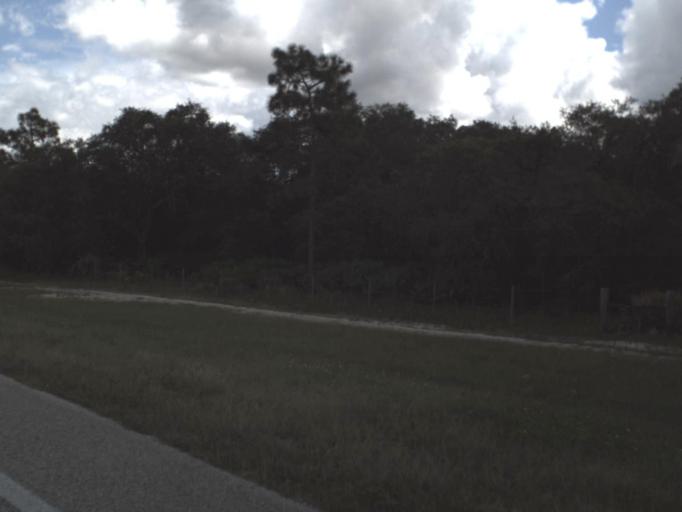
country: US
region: Florida
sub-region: Polk County
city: Lake Wales
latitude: 27.8940
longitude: -81.5295
